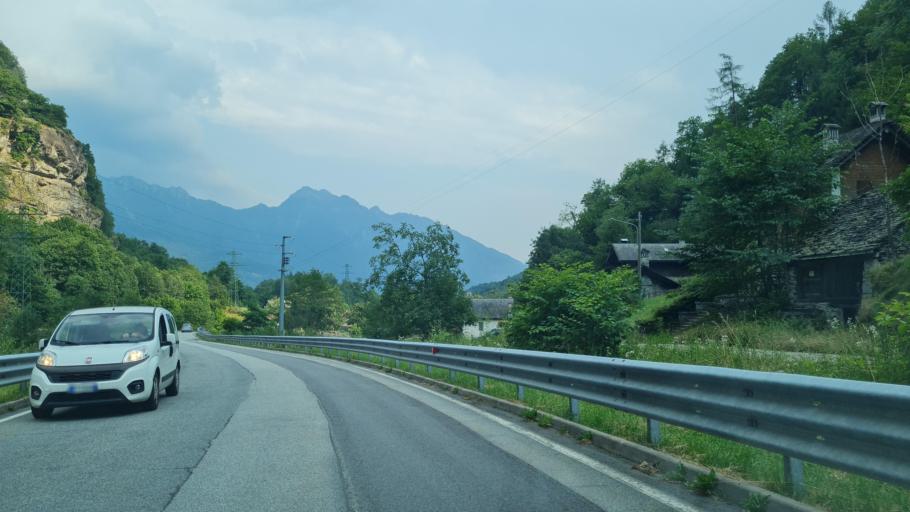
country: IT
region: Piedmont
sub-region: Provincia Verbano-Cusio-Ossola
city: Baceno
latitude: 46.2791
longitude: 8.2954
